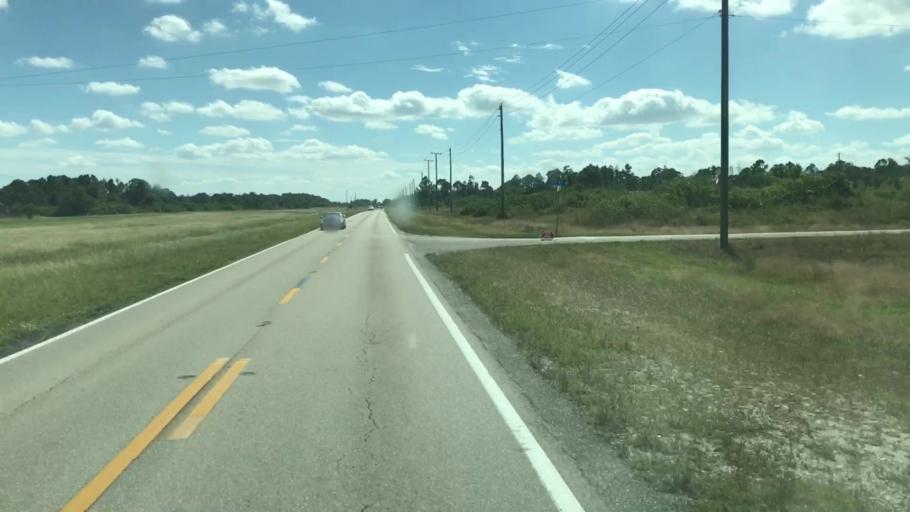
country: US
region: Florida
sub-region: Lee County
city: Lehigh Acres
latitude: 26.6595
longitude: -81.6635
